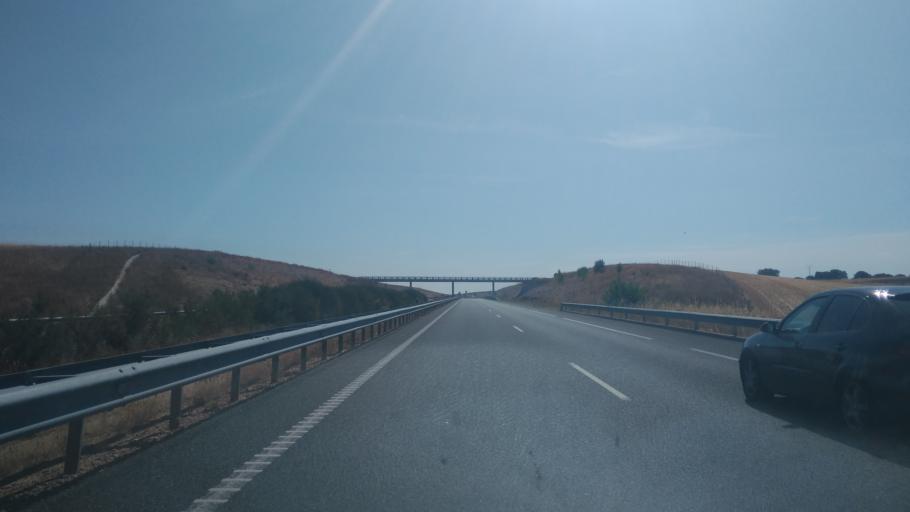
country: ES
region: Castille and Leon
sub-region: Provincia de Salamanca
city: Calvarrasa de Abajo
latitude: 40.9311
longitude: -5.5532
